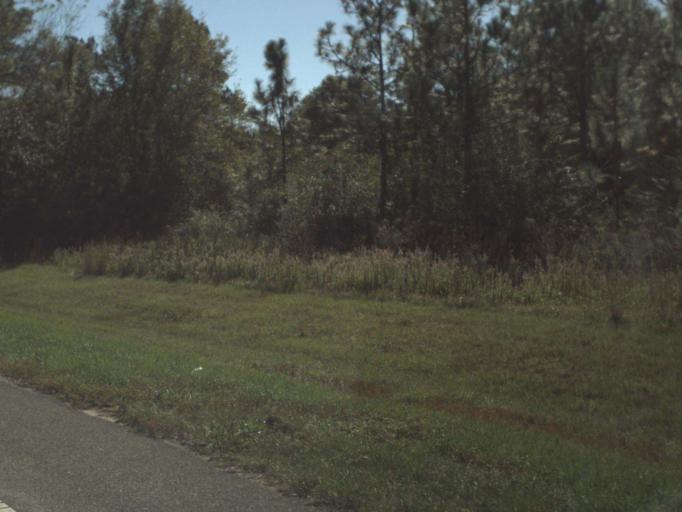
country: US
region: Florida
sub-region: Okaloosa County
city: Crestview
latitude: 30.8113
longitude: -86.7089
